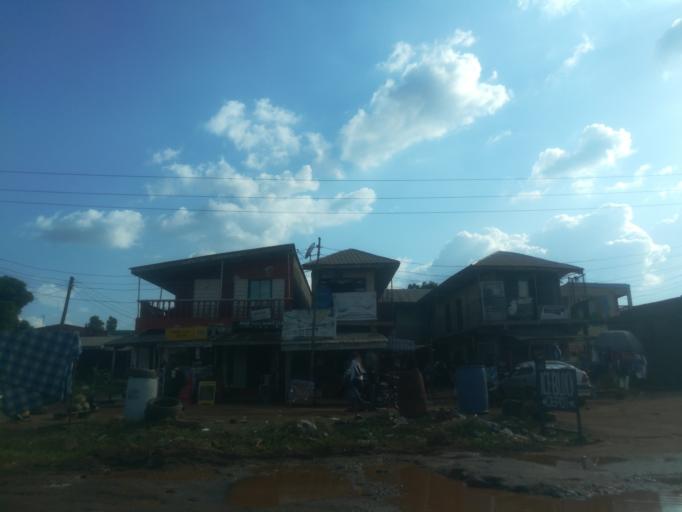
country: NG
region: Oyo
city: Ibadan
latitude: 7.3911
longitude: 3.9714
